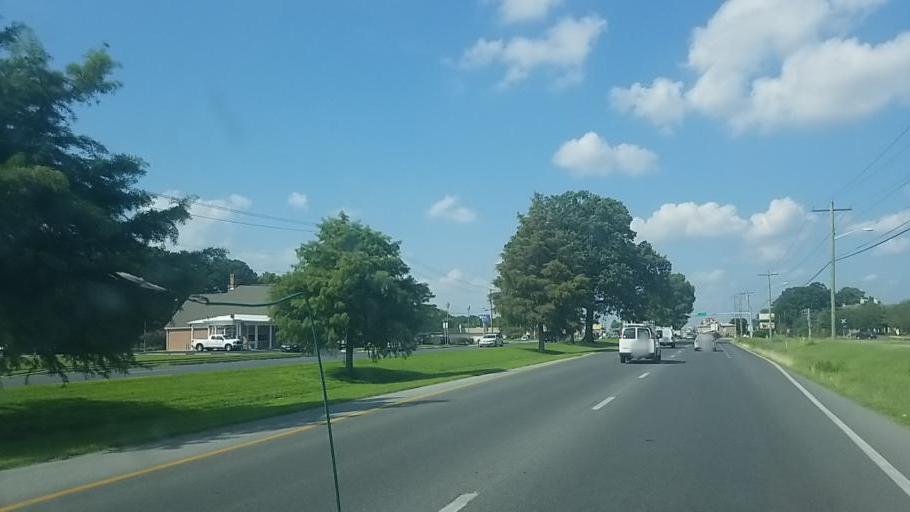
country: US
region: Maryland
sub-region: Wicomico County
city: Fruitland
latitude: 38.3355
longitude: -75.6088
